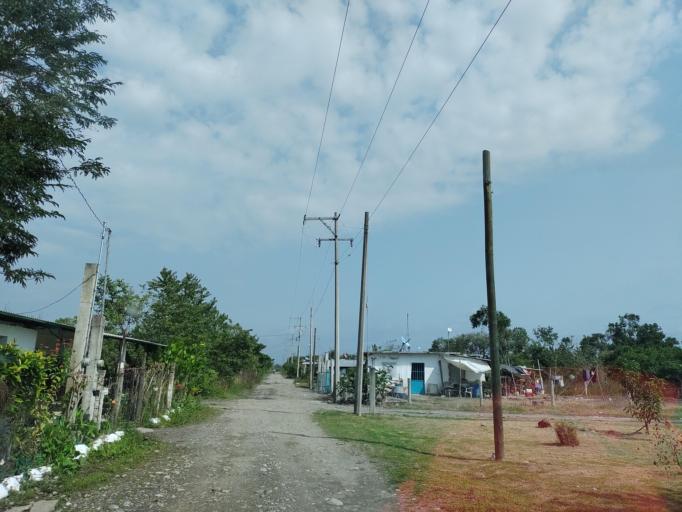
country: MX
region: Puebla
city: Espinal
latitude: 20.2781
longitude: -97.3330
